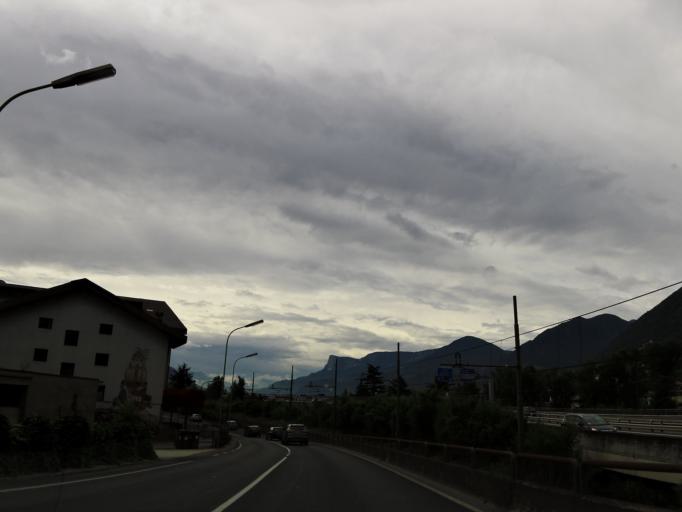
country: IT
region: Trentino-Alto Adige
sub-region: Bolzano
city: Marlengo
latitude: 46.6580
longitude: 11.1464
